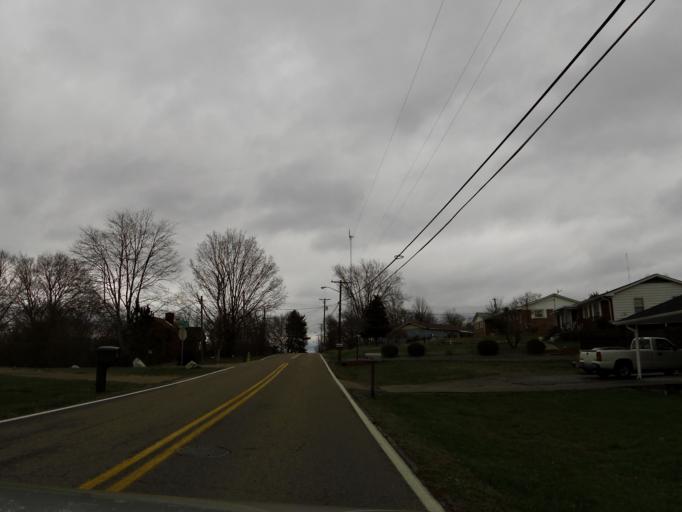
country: US
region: Tennessee
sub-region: Knox County
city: Knoxville
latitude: 35.9973
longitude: -83.9762
